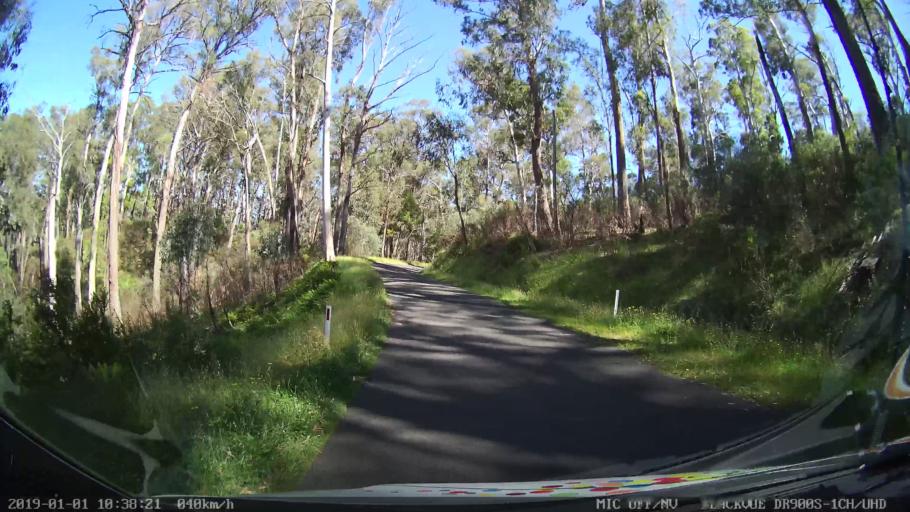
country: AU
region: New South Wales
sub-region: Snowy River
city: Jindabyne
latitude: -36.0459
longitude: 148.3011
